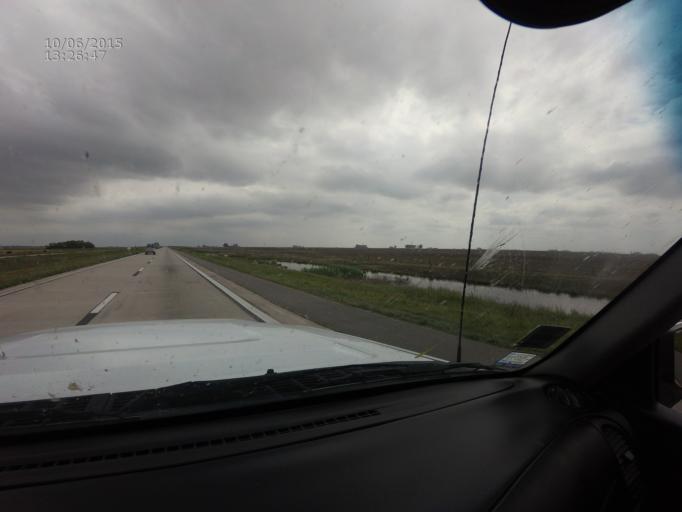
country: AR
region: Cordoba
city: Marcos Juarez
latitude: -32.6482
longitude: -62.1886
